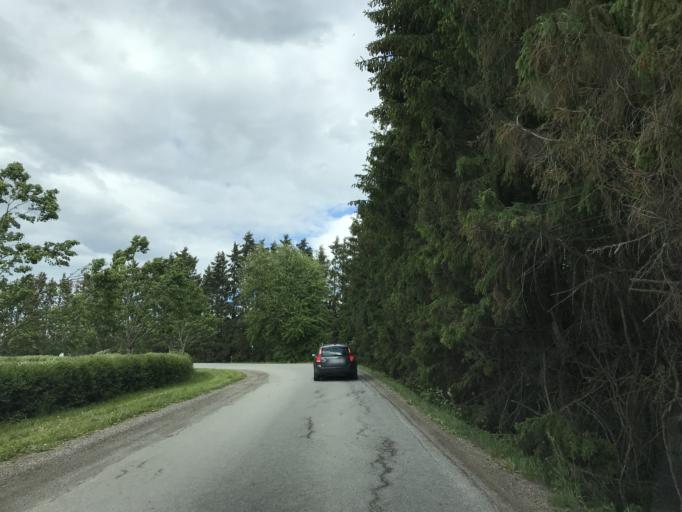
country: SE
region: Stockholm
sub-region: Norrtalje Kommun
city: Bergshamra
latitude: 59.3911
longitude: 18.0064
